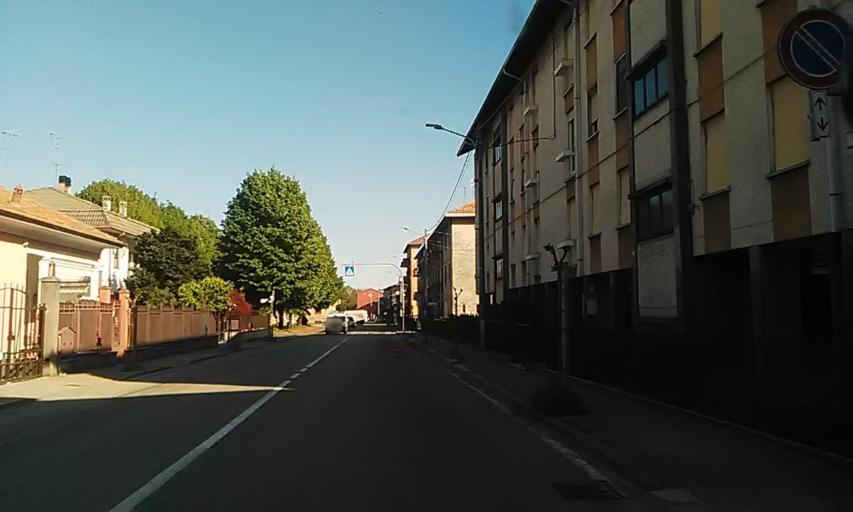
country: IT
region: Piedmont
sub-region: Provincia di Novara
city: Romagnano Sesia
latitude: 45.6296
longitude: 8.3895
